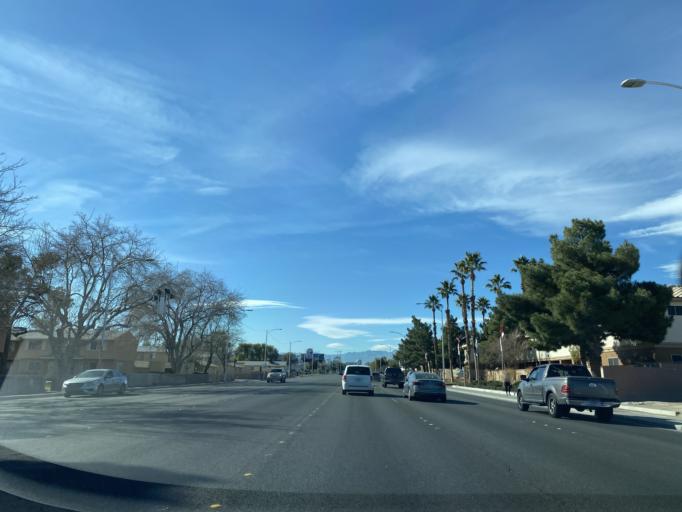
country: US
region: Nevada
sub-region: Clark County
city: North Las Vegas
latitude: 36.1735
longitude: -115.0932
